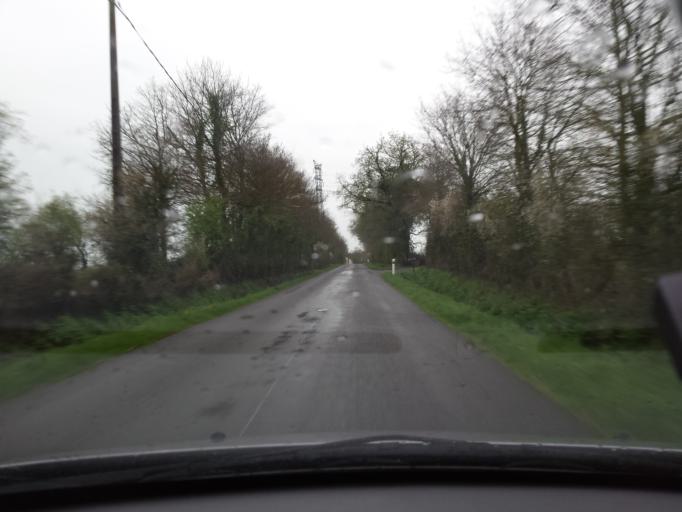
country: FR
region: Pays de la Loire
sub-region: Departement de la Vendee
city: Chauche
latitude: 46.7765
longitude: -1.3037
